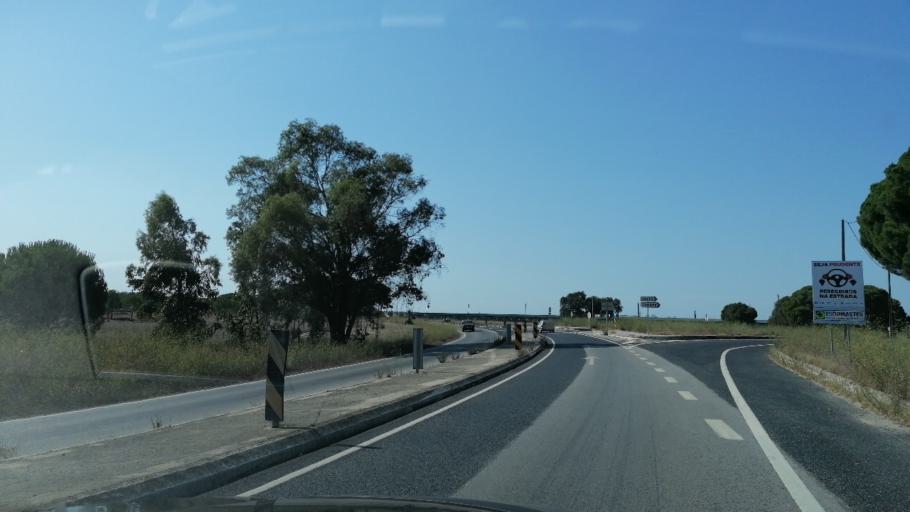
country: PT
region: Evora
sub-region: Vendas Novas
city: Vendas Novas
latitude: 38.7162
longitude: -8.6177
